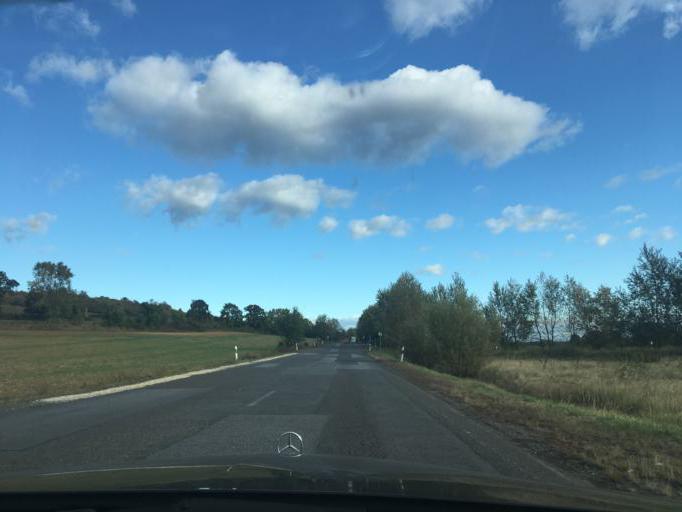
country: HU
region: Borsod-Abauj-Zemplen
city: Encs
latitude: 48.4221
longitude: 21.1798
